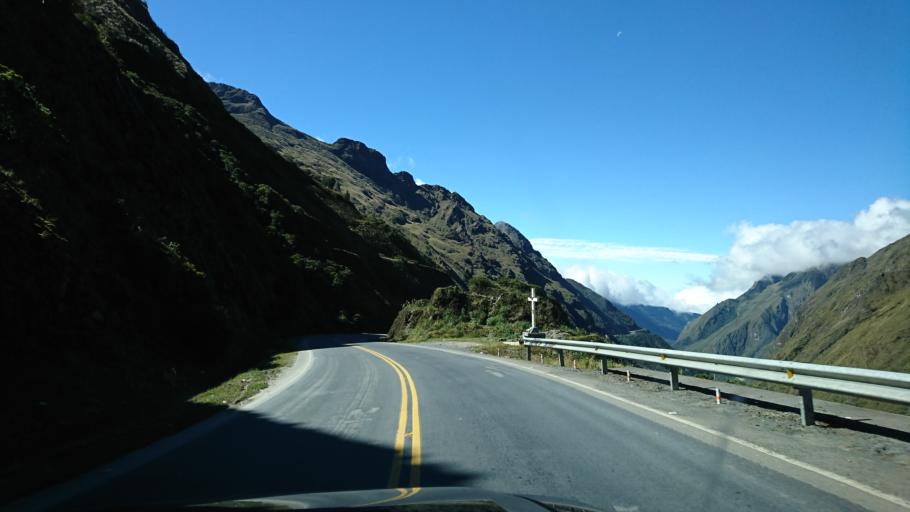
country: BO
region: La Paz
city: Coroico
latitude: -16.3191
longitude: -67.9302
